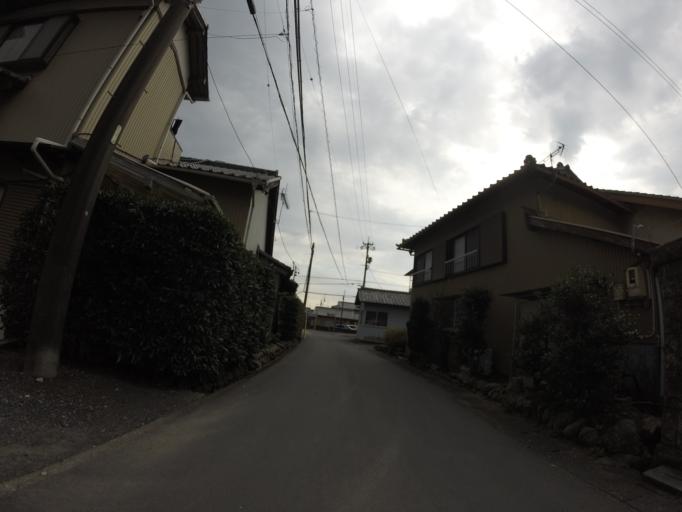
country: JP
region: Shizuoka
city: Shizuoka-shi
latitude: 35.0411
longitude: 138.4495
